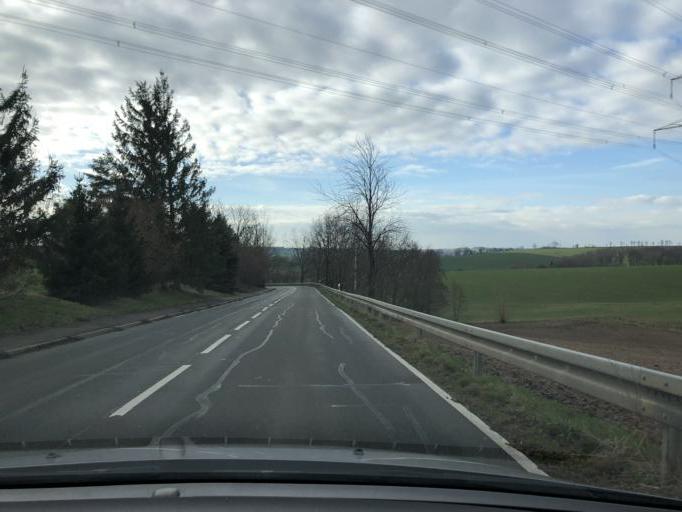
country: DE
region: Saxony
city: Dobeln
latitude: 51.1465
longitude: 13.0898
